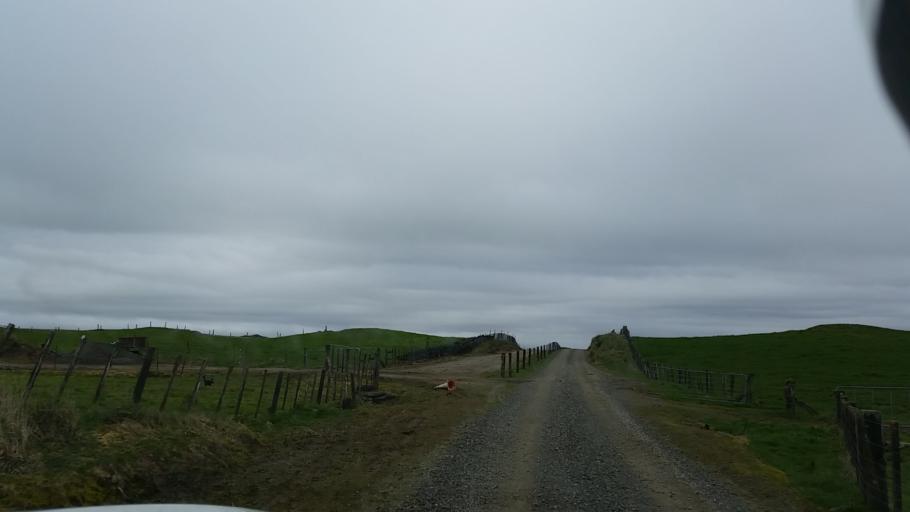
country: NZ
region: Bay of Plenty
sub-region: Rotorua District
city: Rotorua
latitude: -38.1109
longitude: 176.0519
